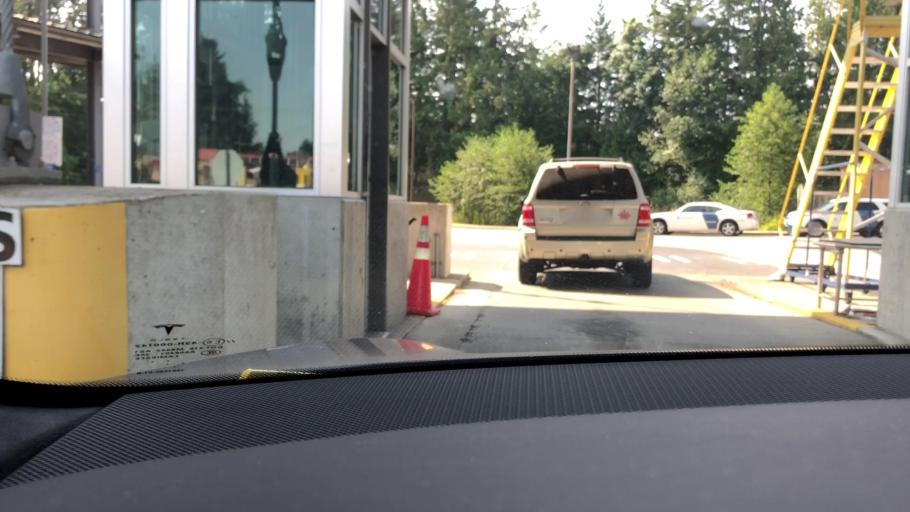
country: US
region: Washington
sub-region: Whatcom County
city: Point Roberts
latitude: 49.0013
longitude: -123.0685
